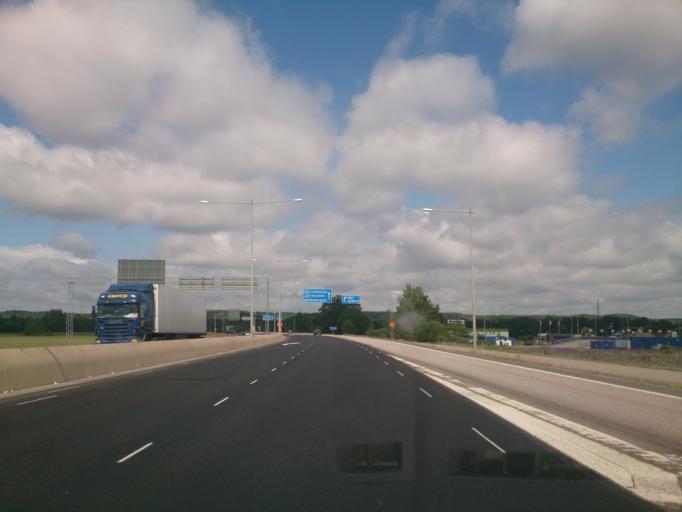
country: SE
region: OEstergoetland
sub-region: Norrkopings Kommun
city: Jursla
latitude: 58.6525
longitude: 16.1689
